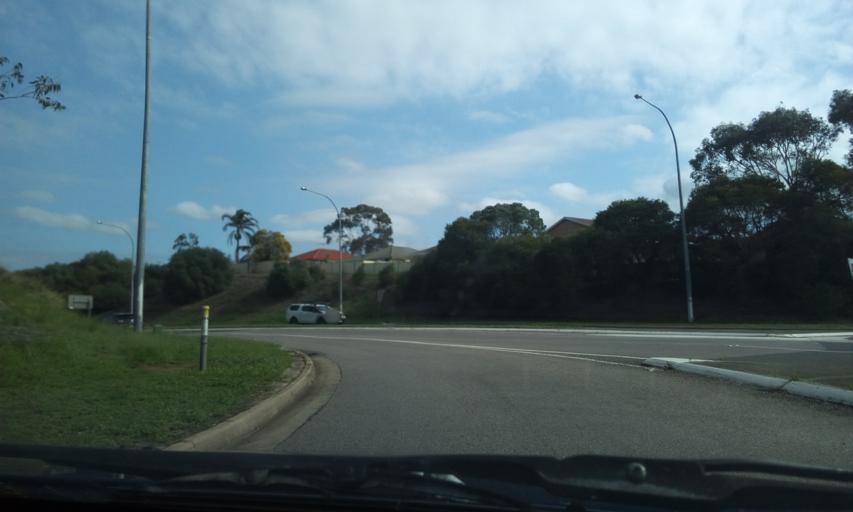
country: AU
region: New South Wales
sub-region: Campbelltown Municipality
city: Glen Alpine
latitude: -34.0787
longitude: 150.7981
